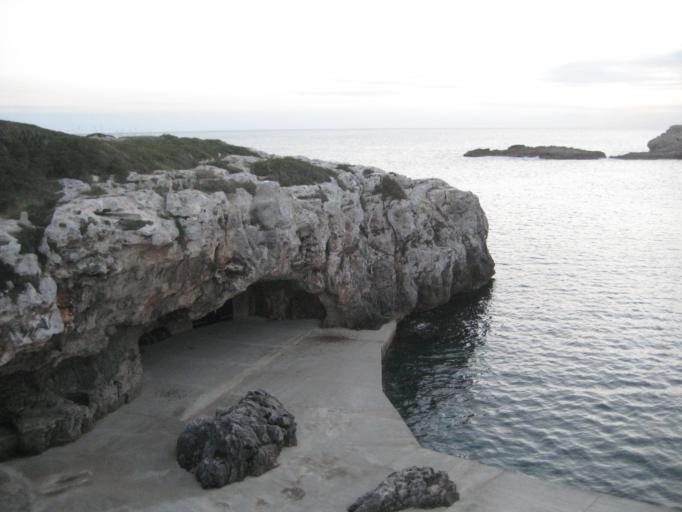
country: ES
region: Balearic Islands
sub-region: Illes Balears
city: Sant Lluis
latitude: 39.8233
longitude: 4.2300
